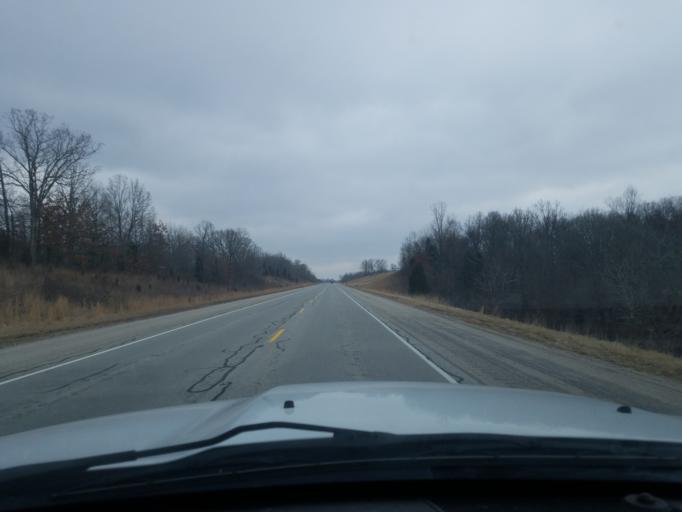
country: US
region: Indiana
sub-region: Perry County
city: Tell City
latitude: 38.0299
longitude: -86.6684
